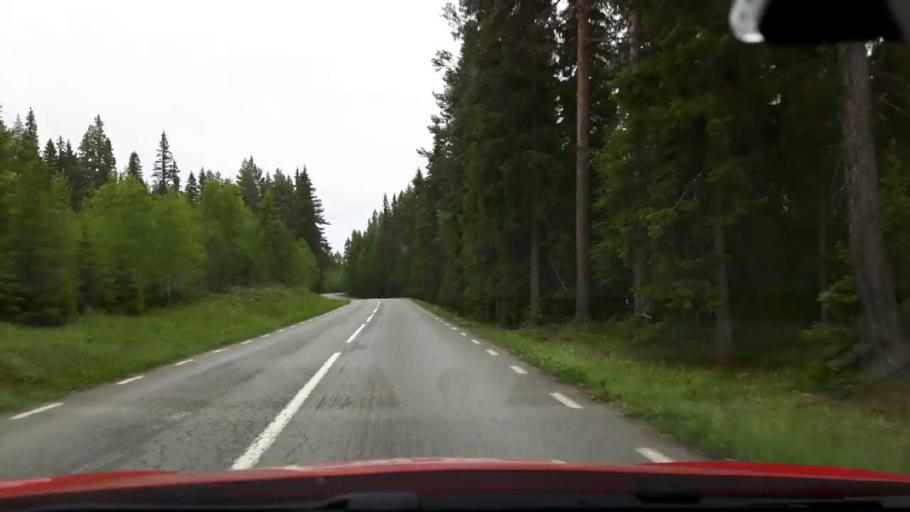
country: SE
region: Jaemtland
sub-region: Stroemsunds Kommun
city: Stroemsund
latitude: 63.4454
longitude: 15.4759
